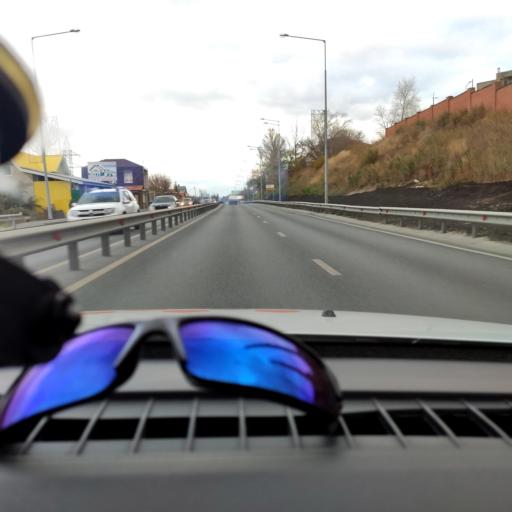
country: RU
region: Samara
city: Volzhskiy
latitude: 53.3787
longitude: 50.1698
